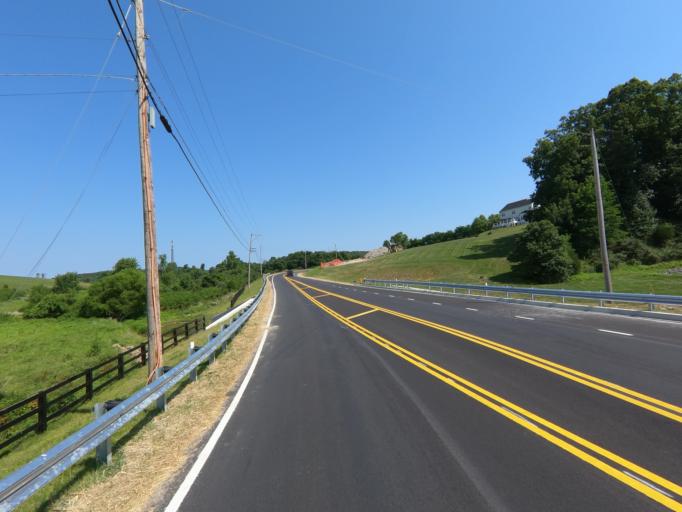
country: US
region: Maryland
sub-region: Frederick County
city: Spring Ridge
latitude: 39.3897
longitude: -77.3250
